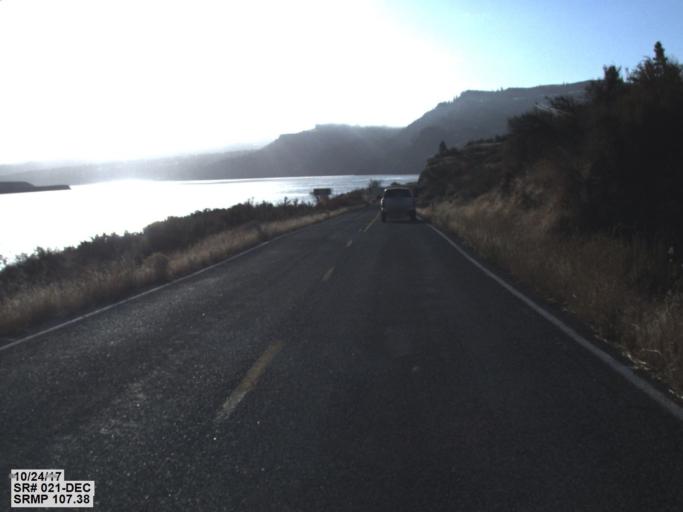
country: US
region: Washington
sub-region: Okanogan County
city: Coulee Dam
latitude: 47.9563
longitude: -118.6948
